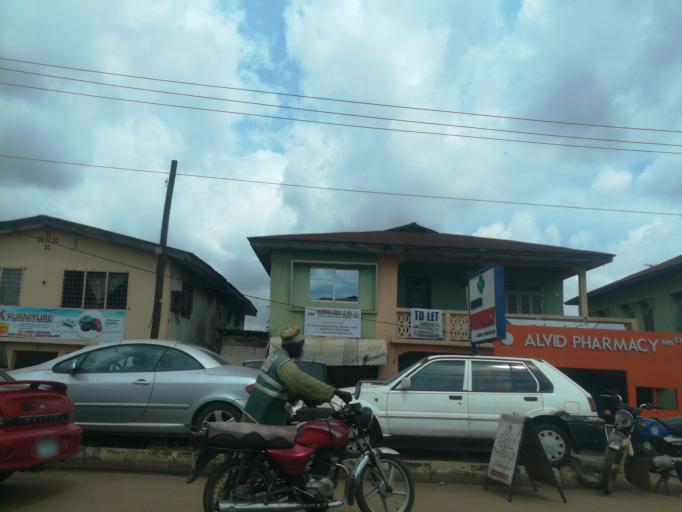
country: NG
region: Oyo
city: Ibadan
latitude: 7.3658
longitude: 3.8846
